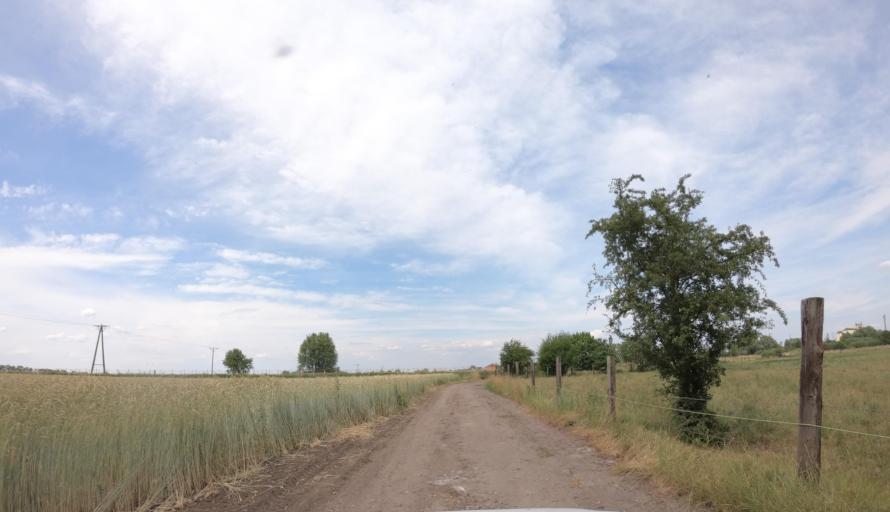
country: PL
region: West Pomeranian Voivodeship
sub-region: Powiat pyrzycki
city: Pyrzyce
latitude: 53.1398
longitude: 14.8696
